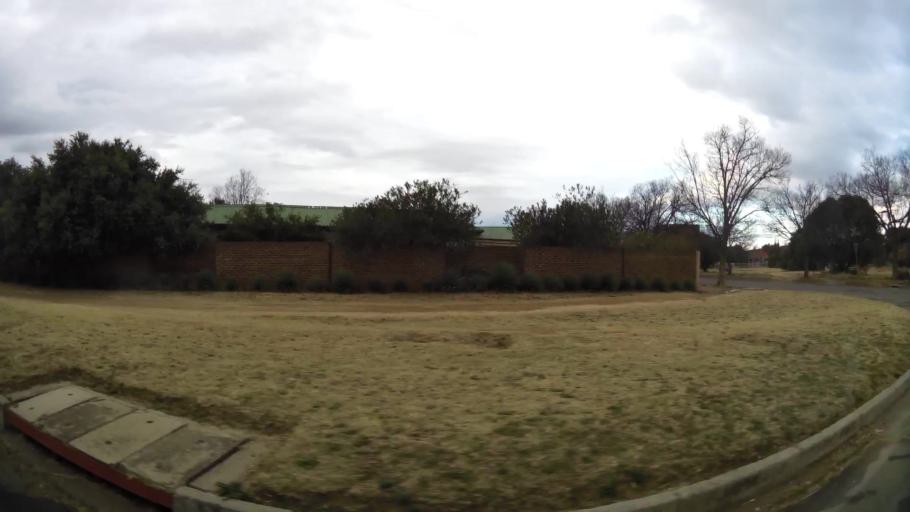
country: ZA
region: Orange Free State
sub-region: Lejweleputswa District Municipality
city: Welkom
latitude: -27.9653
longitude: 26.7262
